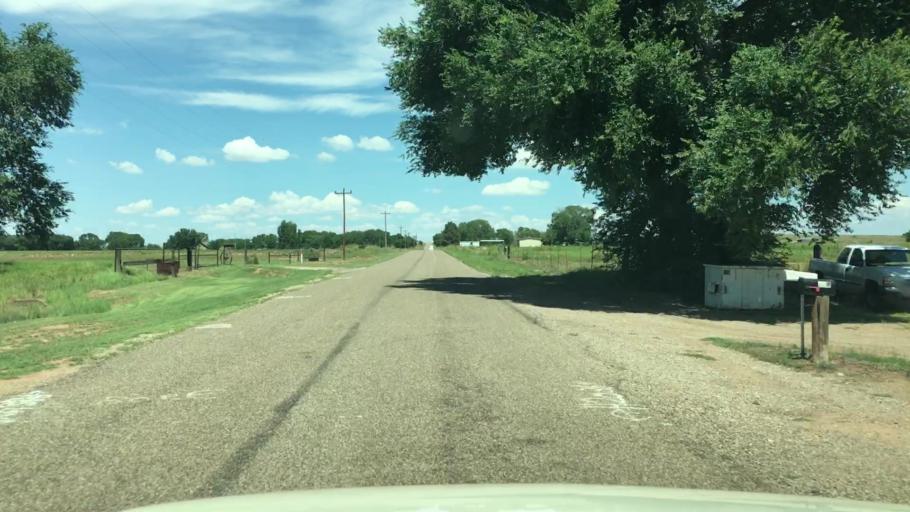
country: US
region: New Mexico
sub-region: De Baca County
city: Fort Sumner
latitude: 34.4416
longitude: -104.1936
